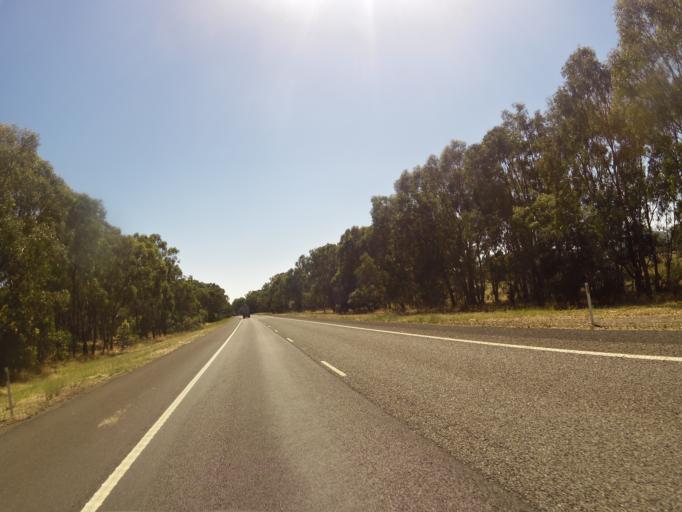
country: AU
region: Victoria
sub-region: Greater Shepparton
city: Shepparton
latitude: -36.7907
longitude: 145.4880
